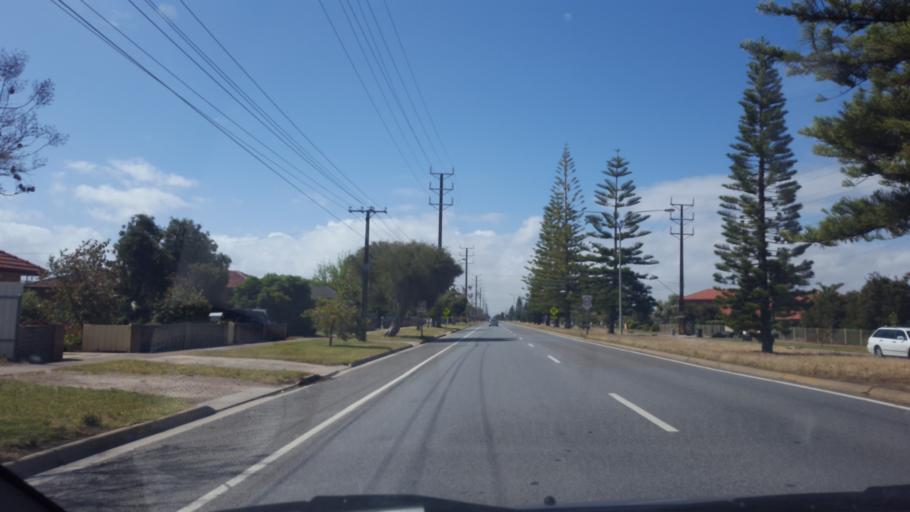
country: AU
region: South Australia
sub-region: Port Adelaide Enfield
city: Birkenhead
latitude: -34.8156
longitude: 138.5012
